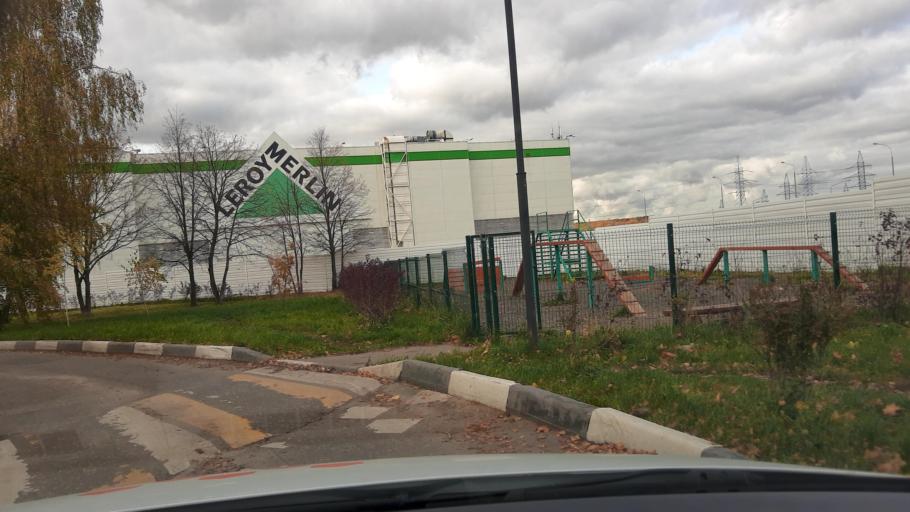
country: RU
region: Moskovskaya
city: Razvilka
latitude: 55.5893
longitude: 37.7293
